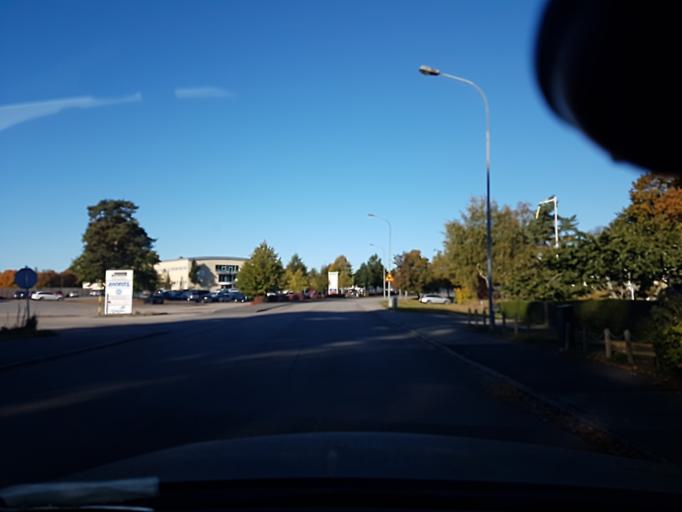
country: SE
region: Kronoberg
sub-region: Vaxjo Kommun
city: Vaexjoe
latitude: 56.8713
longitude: 14.8311
